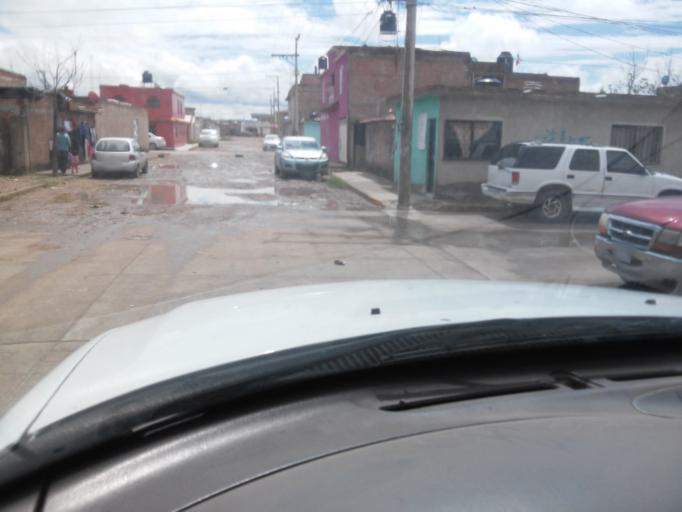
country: MX
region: Durango
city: Victoria de Durango
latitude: 24.0164
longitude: -104.6073
